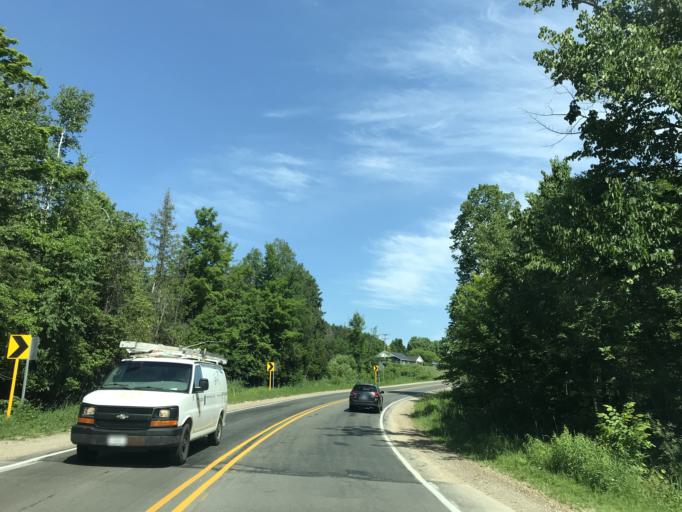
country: US
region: Michigan
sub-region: Grand Traverse County
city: Traverse City
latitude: 44.6992
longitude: -85.6250
